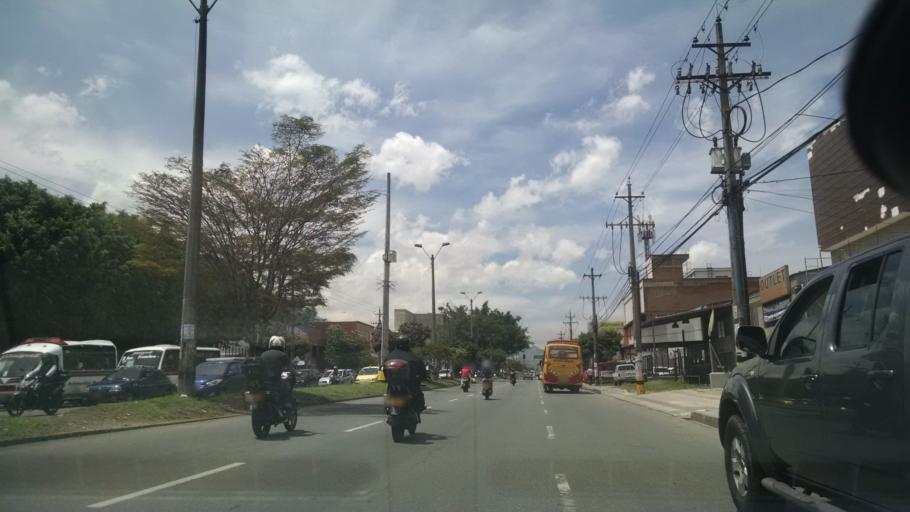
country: CO
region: Antioquia
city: Itagui
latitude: 6.2025
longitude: -75.5879
